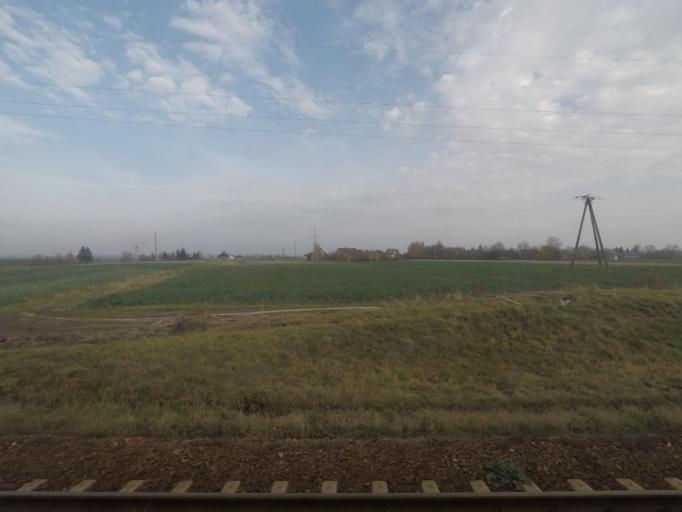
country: PL
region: Subcarpathian Voivodeship
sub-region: Powiat jaroslawski
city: Radymno
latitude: 49.9297
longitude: 22.8389
